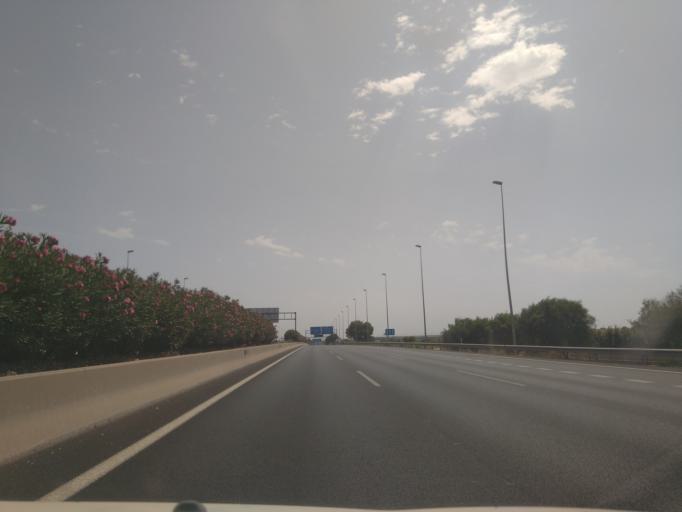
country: ES
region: Valencia
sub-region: Provincia de Valencia
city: Silla
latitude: 39.3616
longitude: -0.4262
